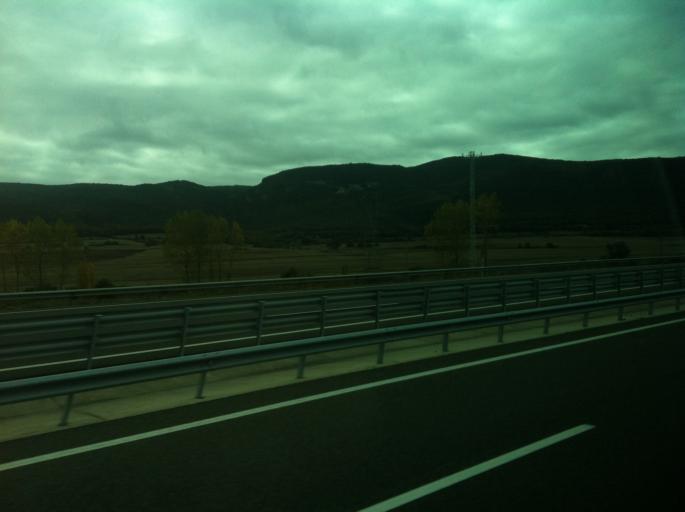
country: ES
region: Castille and Leon
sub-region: Provincia de Burgos
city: Ameyugo
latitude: 42.6591
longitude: -3.0404
